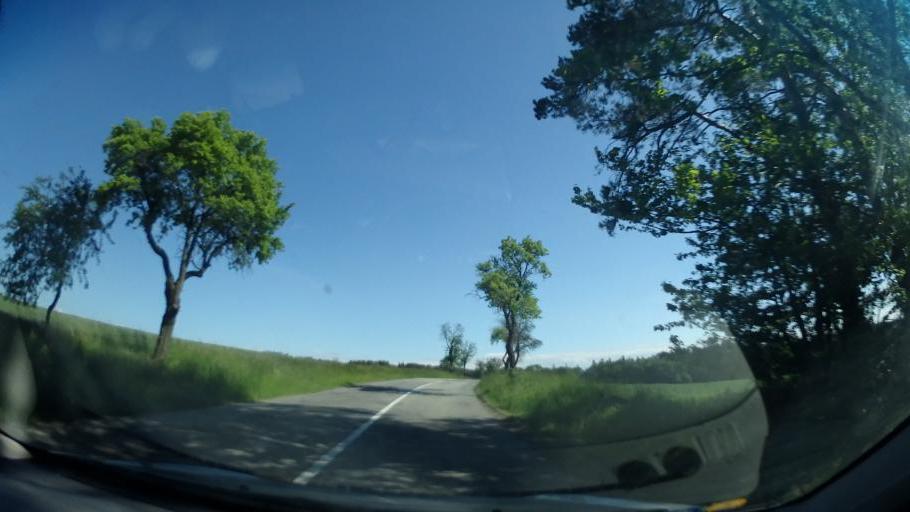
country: CZ
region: South Moravian
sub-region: Okres Blansko
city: Letovice
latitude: 49.5731
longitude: 16.5827
